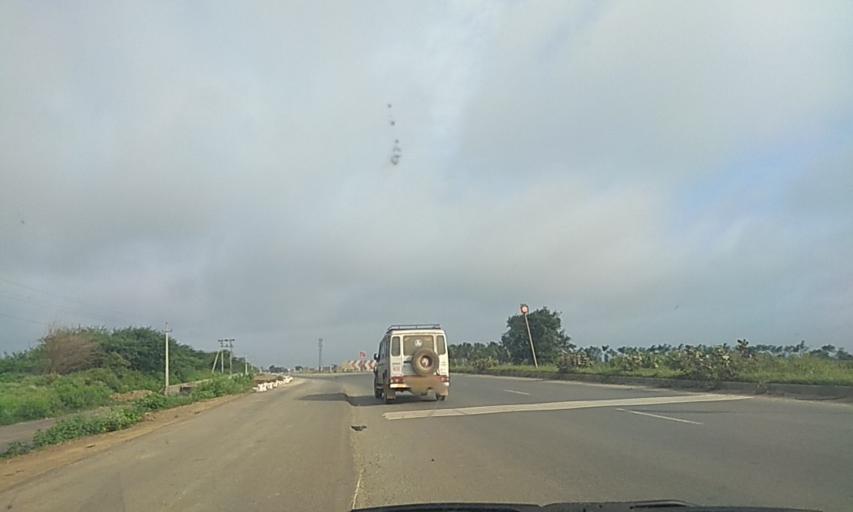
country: IN
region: Karnataka
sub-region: Haveri
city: Haveri
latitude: 14.7697
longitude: 75.4249
